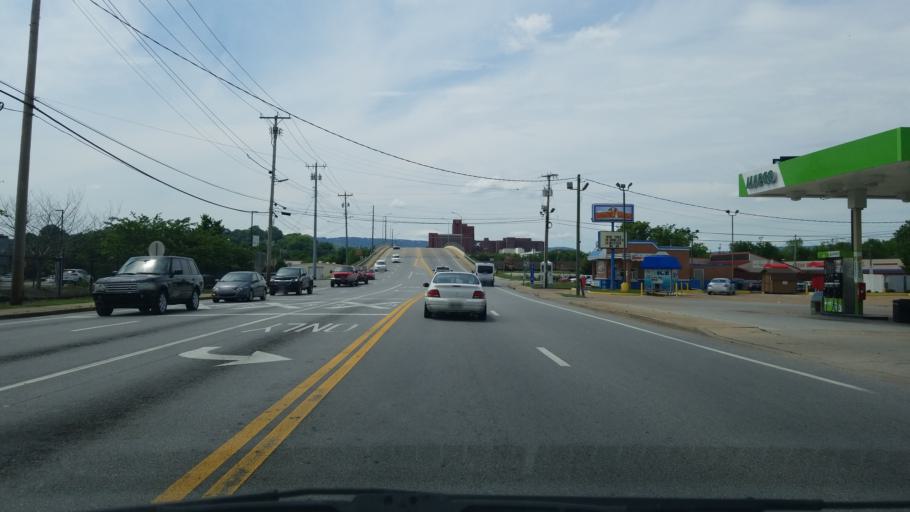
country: US
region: Tennessee
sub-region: Hamilton County
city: Chattanooga
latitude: 35.0439
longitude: -85.2800
